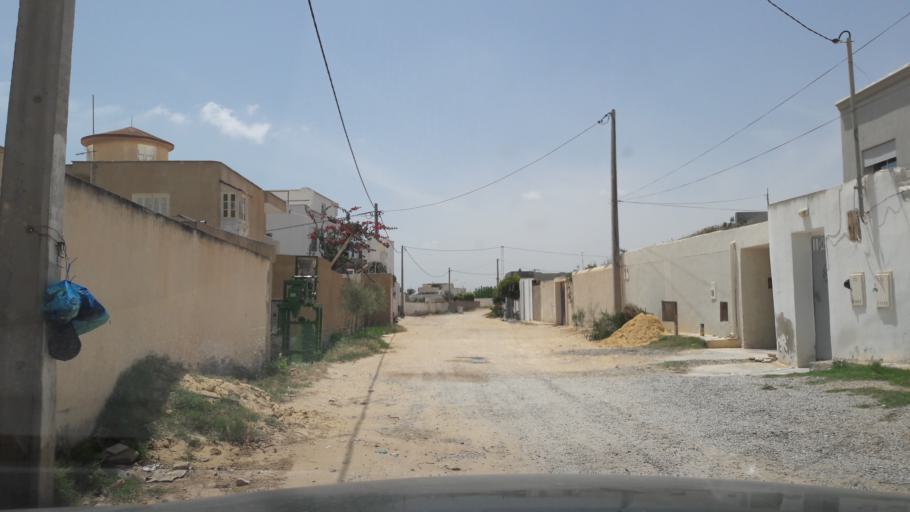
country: TN
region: Safaqis
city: Sfax
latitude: 34.7802
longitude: 10.7571
